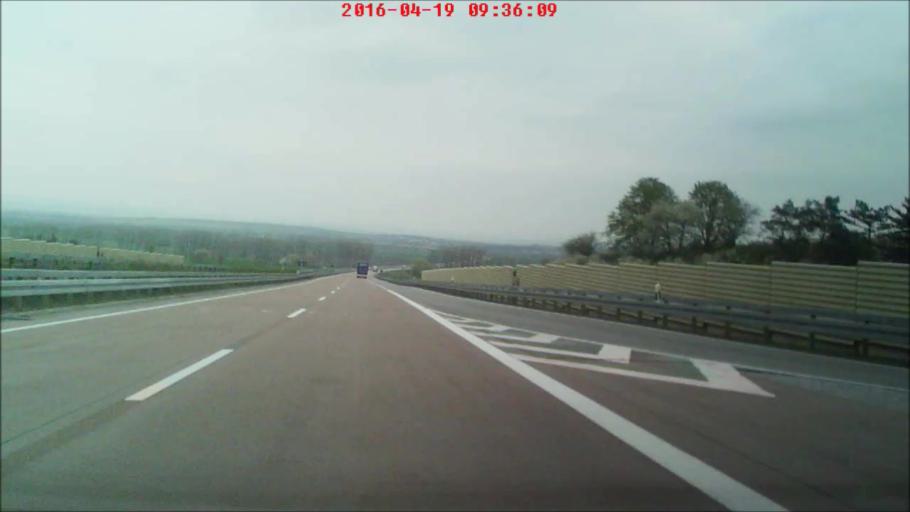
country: DE
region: Thuringia
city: Reinsdorf
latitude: 51.3315
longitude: 11.2525
